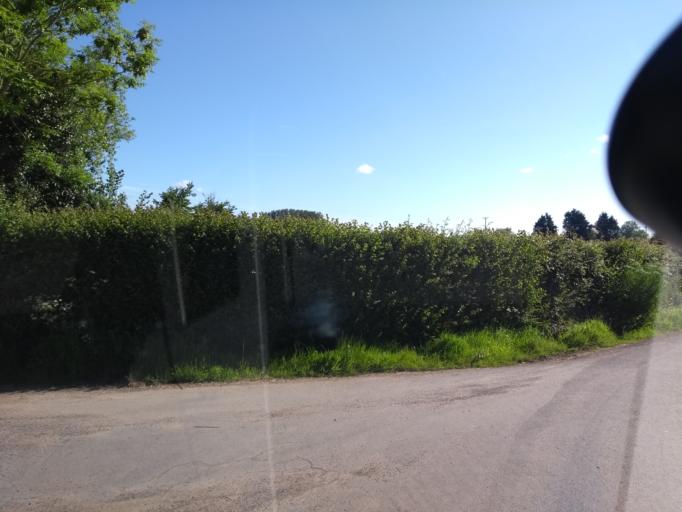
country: GB
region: England
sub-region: Somerset
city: Bridgwater
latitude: 51.1466
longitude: -3.0346
